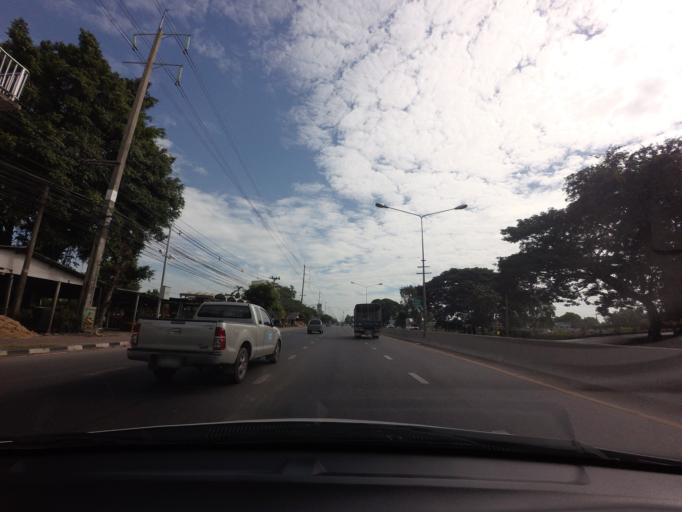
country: TH
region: Pathum Thani
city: Ban Rangsit
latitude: 14.0400
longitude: 100.7870
